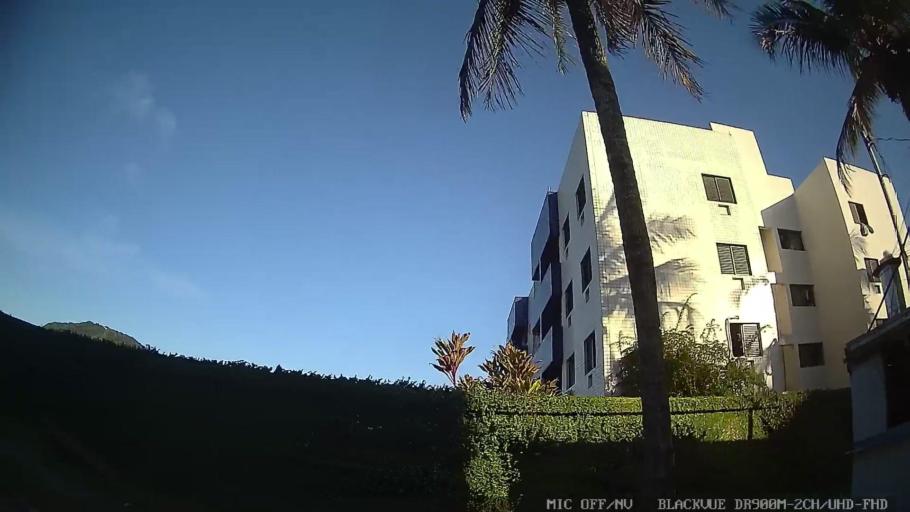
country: BR
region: Sao Paulo
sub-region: Guaruja
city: Guaruja
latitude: -23.9740
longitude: -46.2719
